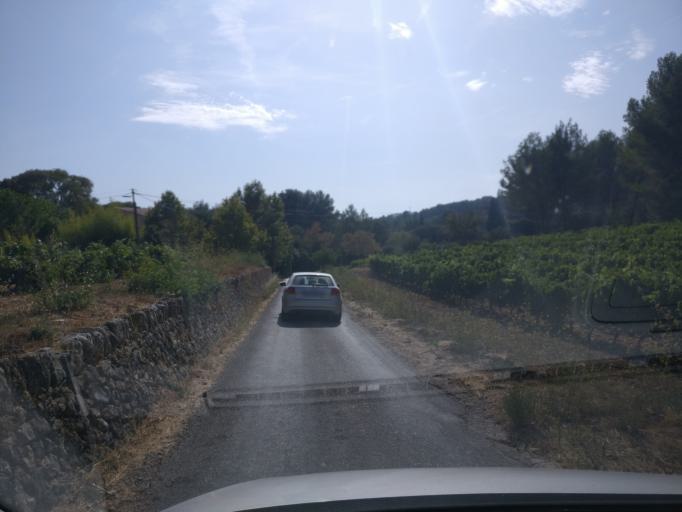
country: FR
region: Provence-Alpes-Cote d'Azur
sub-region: Departement du Var
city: Sanary-sur-Mer
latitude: 43.1504
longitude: 5.7823
